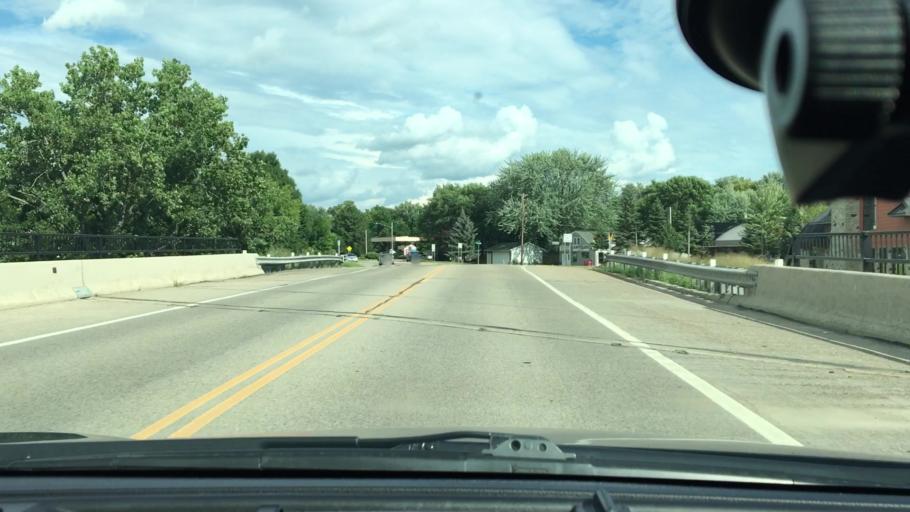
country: US
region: Minnesota
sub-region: Carver County
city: Victoria
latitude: 44.8596
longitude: -93.6657
